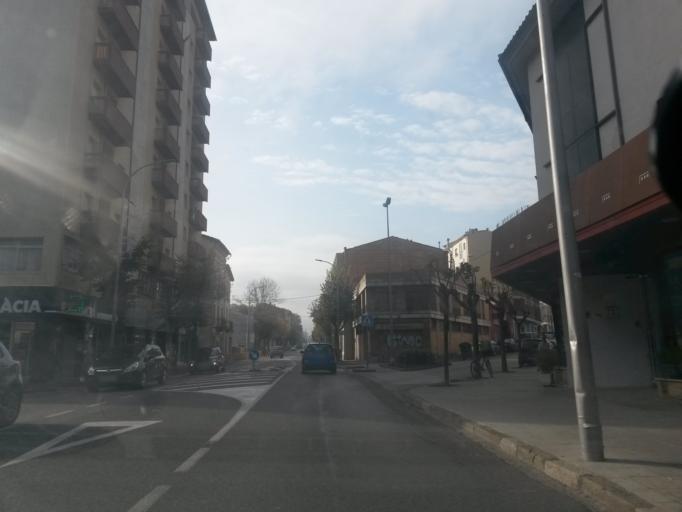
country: ES
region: Catalonia
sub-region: Provincia de Girona
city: Olot
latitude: 42.1758
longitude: 2.4816
